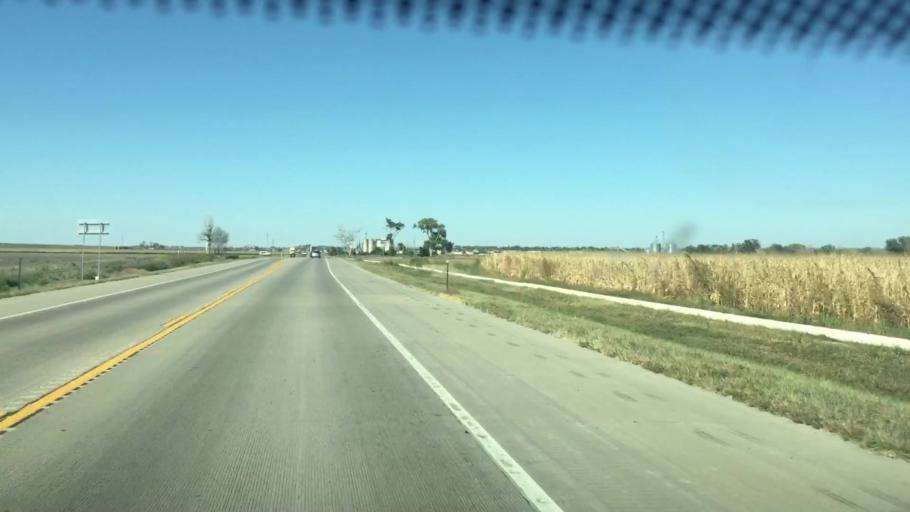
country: US
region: Colorado
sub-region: Prowers County
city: Lamar
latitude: 38.1389
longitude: -102.7237
